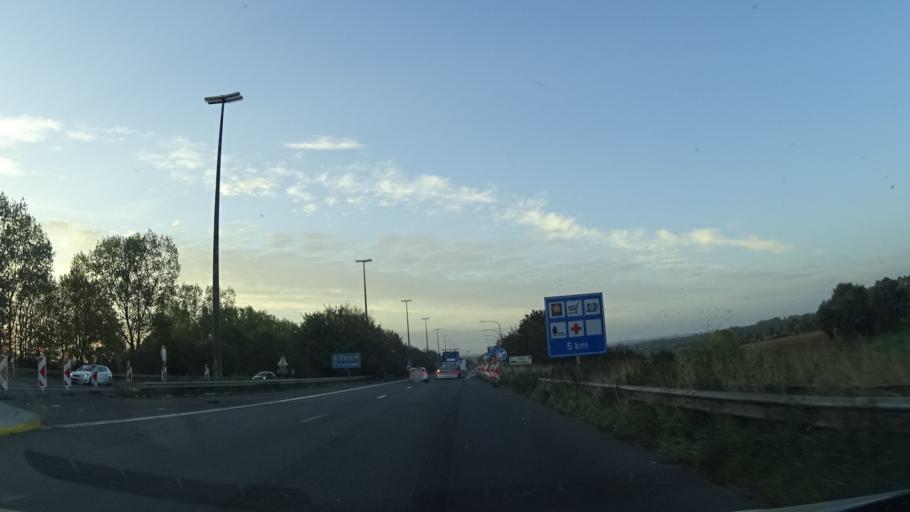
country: BE
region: Wallonia
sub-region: Province du Hainaut
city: Boussu
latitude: 50.4729
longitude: 3.7440
